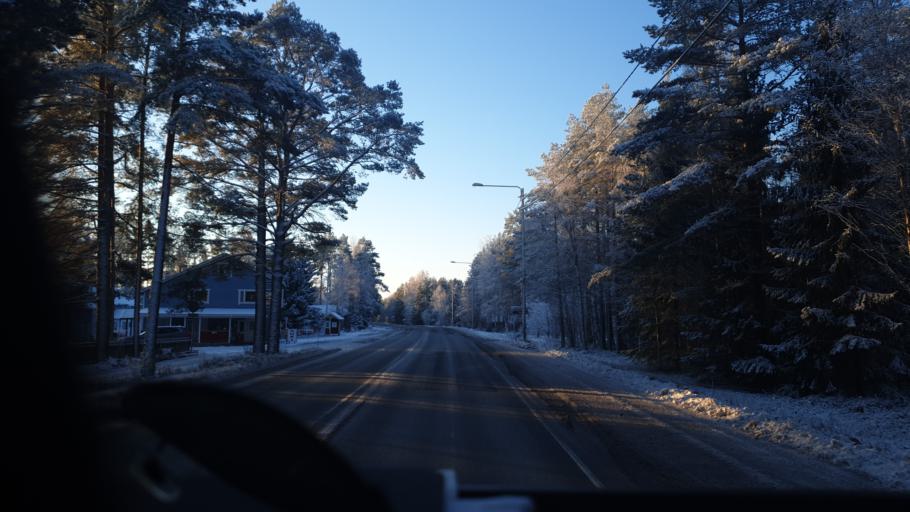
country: FI
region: Northern Ostrobothnia
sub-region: Ylivieska
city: Himanka
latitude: 64.2076
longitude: 23.7664
